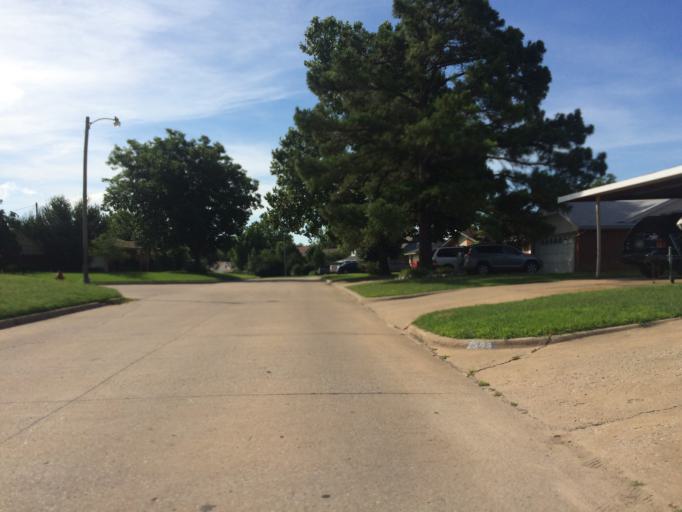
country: US
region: Oklahoma
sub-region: Cleveland County
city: Norman
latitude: 35.2219
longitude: -97.4757
